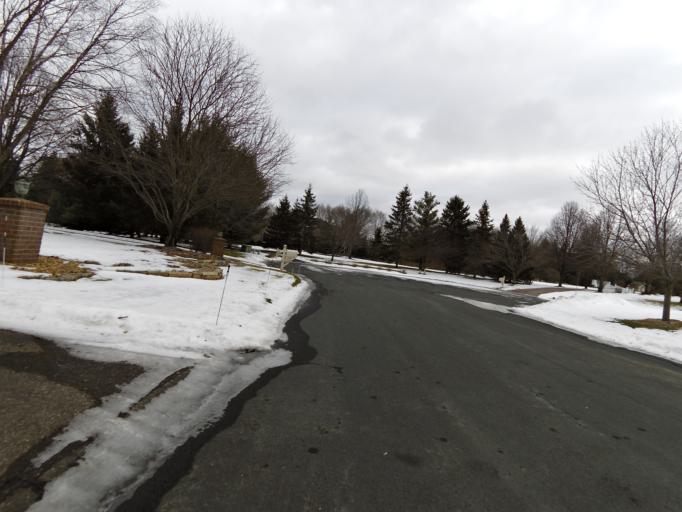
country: US
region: Minnesota
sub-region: Washington County
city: Lake Elmo
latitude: 44.9601
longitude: -92.8341
